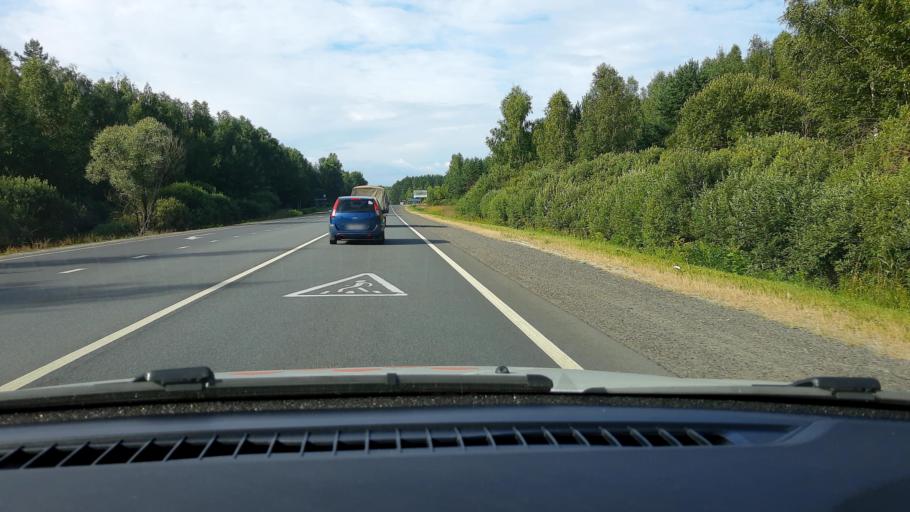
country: RU
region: Nizjnij Novgorod
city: Arzamas
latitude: 55.5176
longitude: 43.9055
